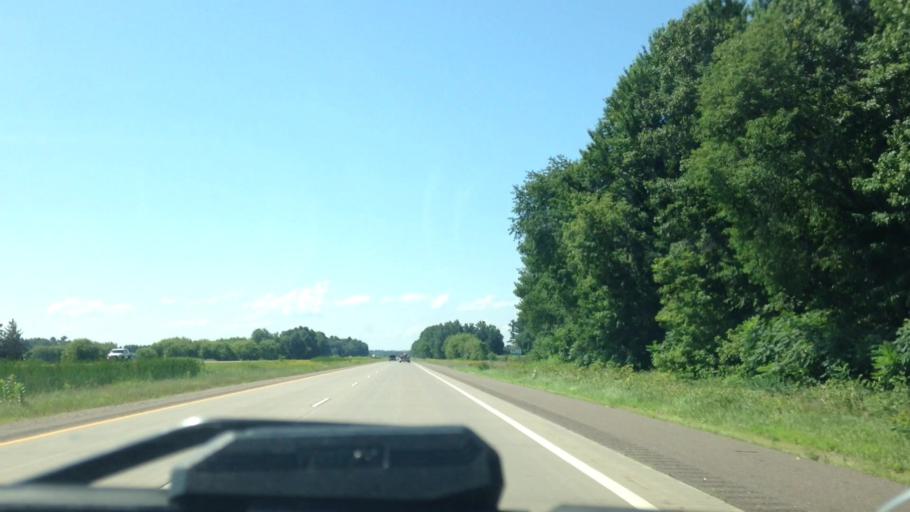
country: US
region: Wisconsin
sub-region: Barron County
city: Cameron
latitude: 45.4385
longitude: -91.7606
